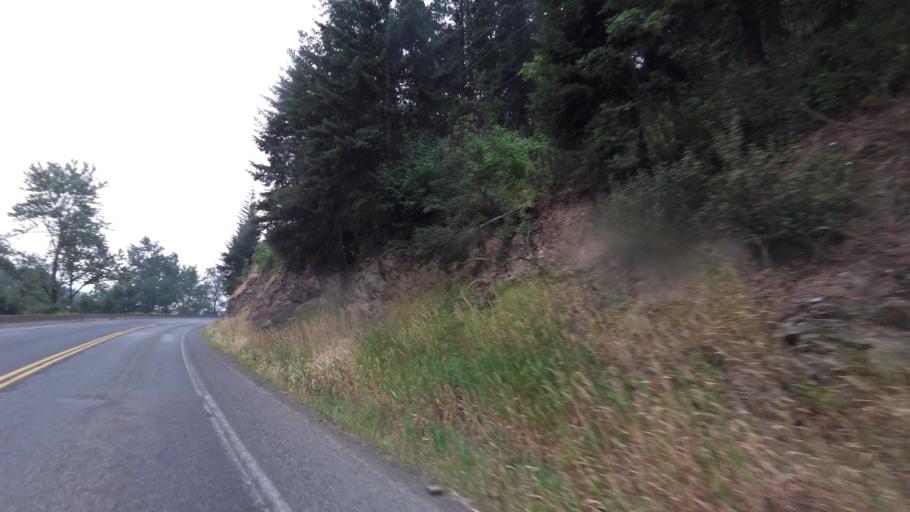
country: CA
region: British Columbia
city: Kamloops
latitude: 51.3981
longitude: -120.2016
